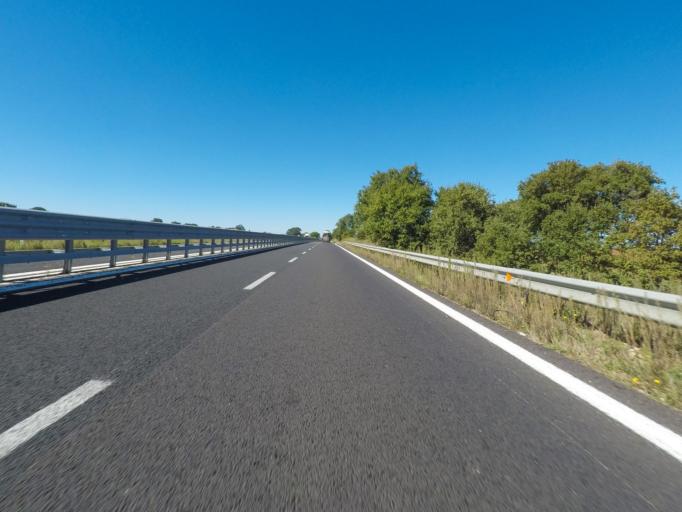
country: IT
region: Latium
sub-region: Provincia di Viterbo
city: Montalto di Castro
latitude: 42.3002
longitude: 11.6711
